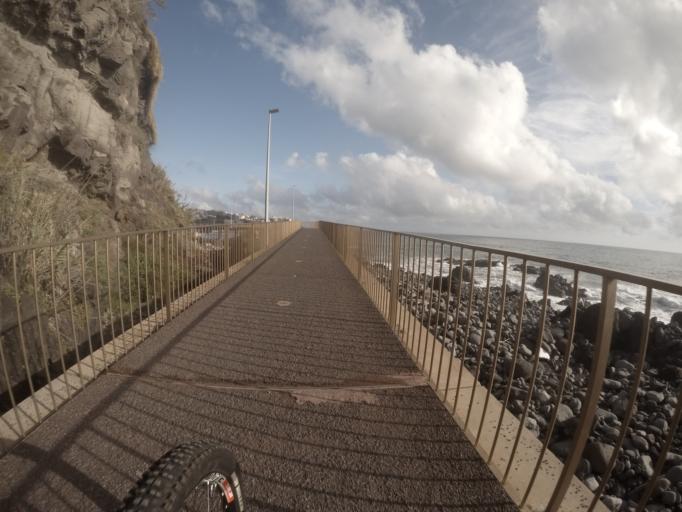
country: PT
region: Madeira
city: Camara de Lobos
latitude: 32.6432
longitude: -16.9625
